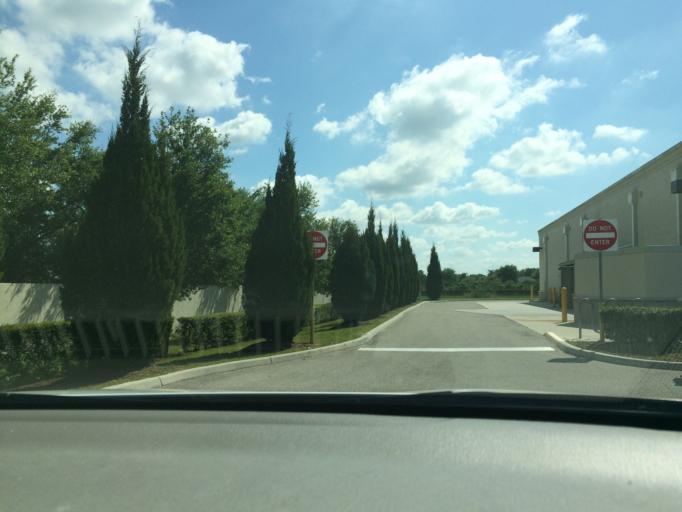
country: US
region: Florida
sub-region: Manatee County
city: Ellenton
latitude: 27.4862
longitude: -82.4337
